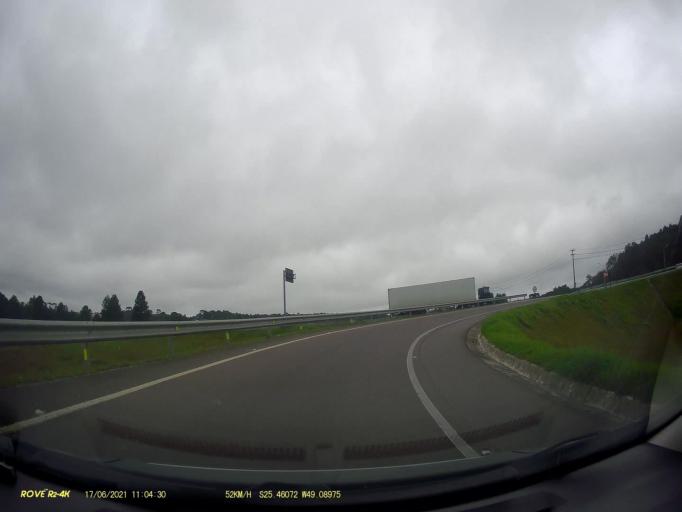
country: BR
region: Parana
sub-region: Piraquara
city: Piraquara
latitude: -25.4604
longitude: -49.0979
